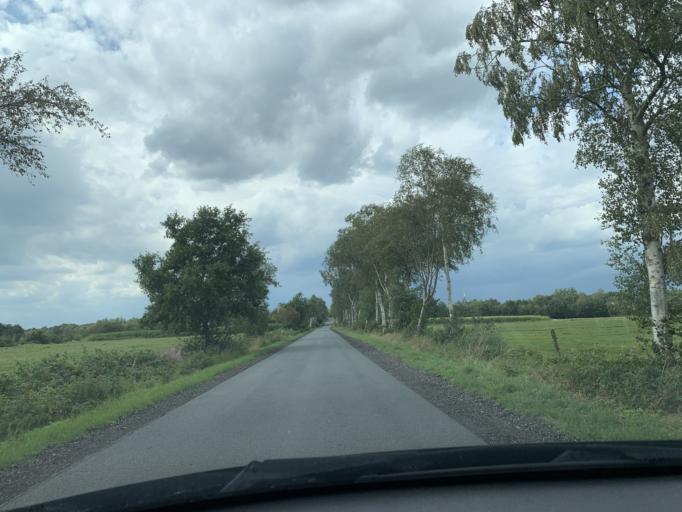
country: DE
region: Lower Saxony
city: Apen
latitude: 53.2742
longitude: 7.8230
